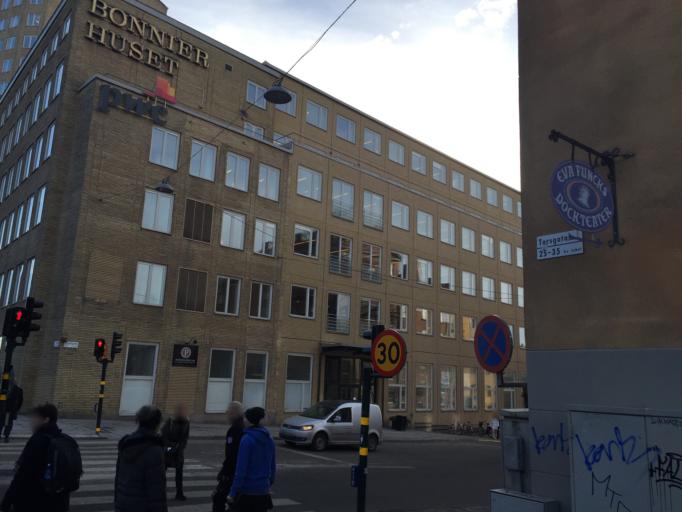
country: SE
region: Stockholm
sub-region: Stockholms Kommun
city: Stockholm
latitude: 59.3382
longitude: 18.0404
